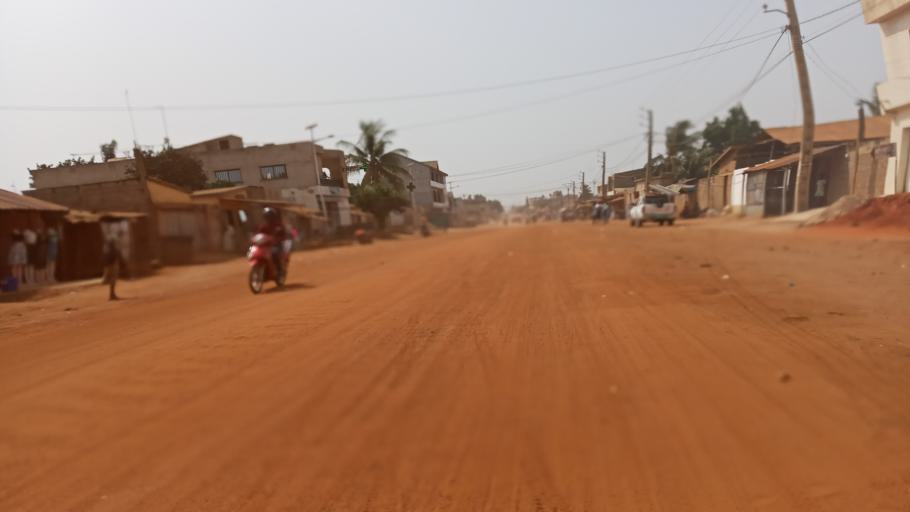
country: TG
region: Maritime
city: Lome
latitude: 6.2024
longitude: 1.1674
